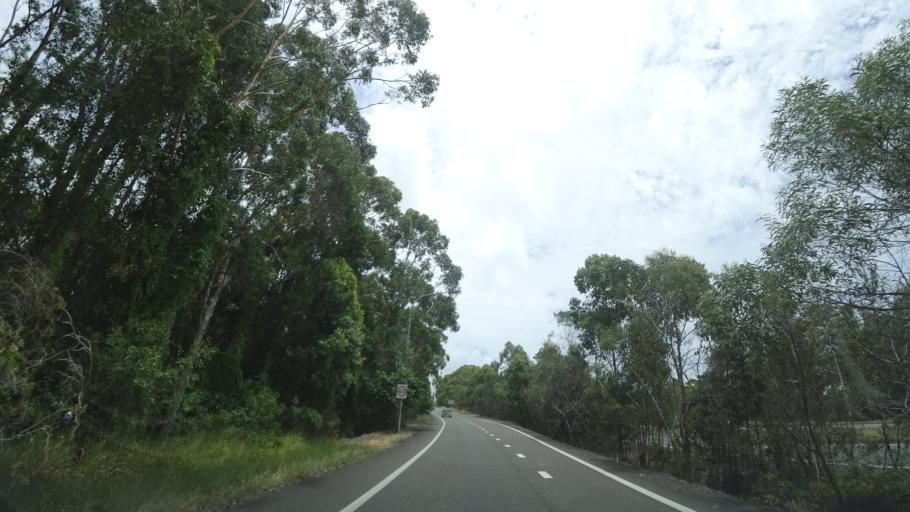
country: AU
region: Queensland
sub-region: Sunshine Coast
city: Mooloolaba
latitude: -26.6775
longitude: 153.0983
